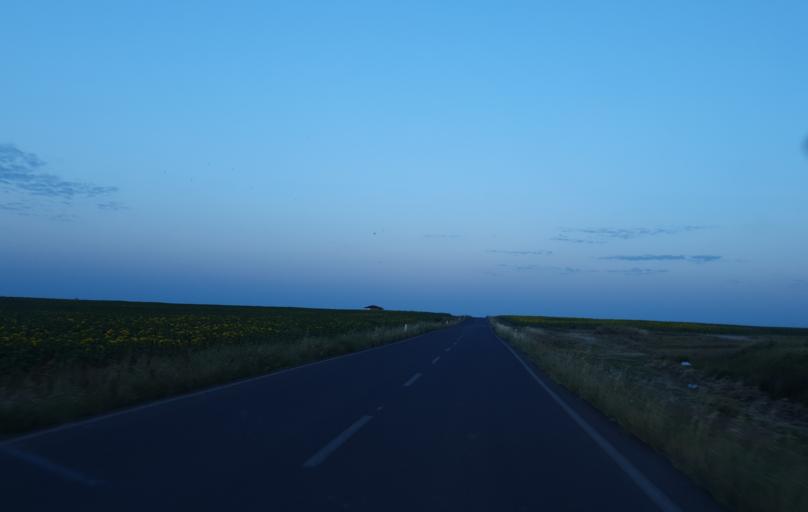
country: TR
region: Tekirdag
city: Velimese
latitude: 41.3363
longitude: 27.9093
